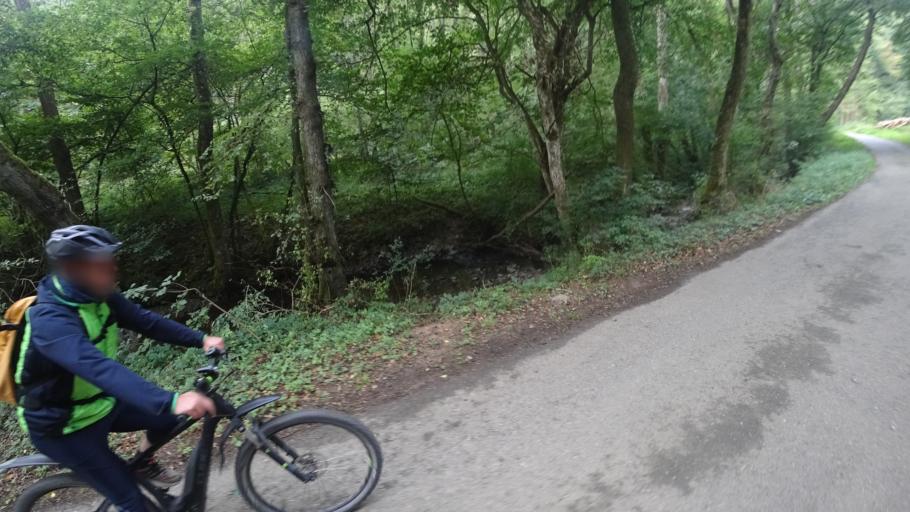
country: DE
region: Rheinland-Pfalz
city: Morshausen
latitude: 50.2065
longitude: 7.4552
